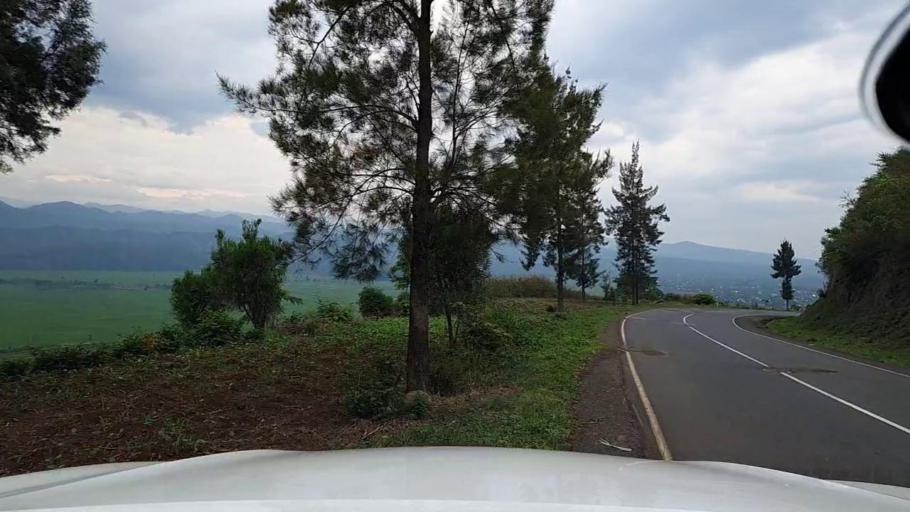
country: RW
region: Western Province
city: Cyangugu
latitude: -2.6755
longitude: 29.0031
